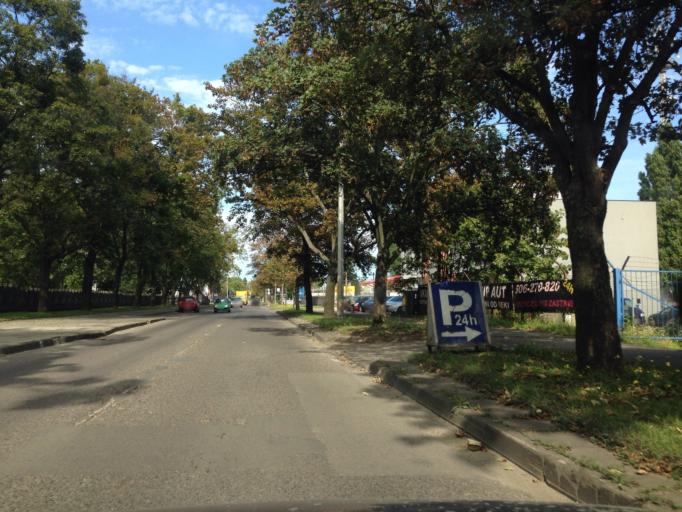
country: PL
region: Pomeranian Voivodeship
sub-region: Gdansk
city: Gdansk
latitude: 54.3932
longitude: 18.6173
